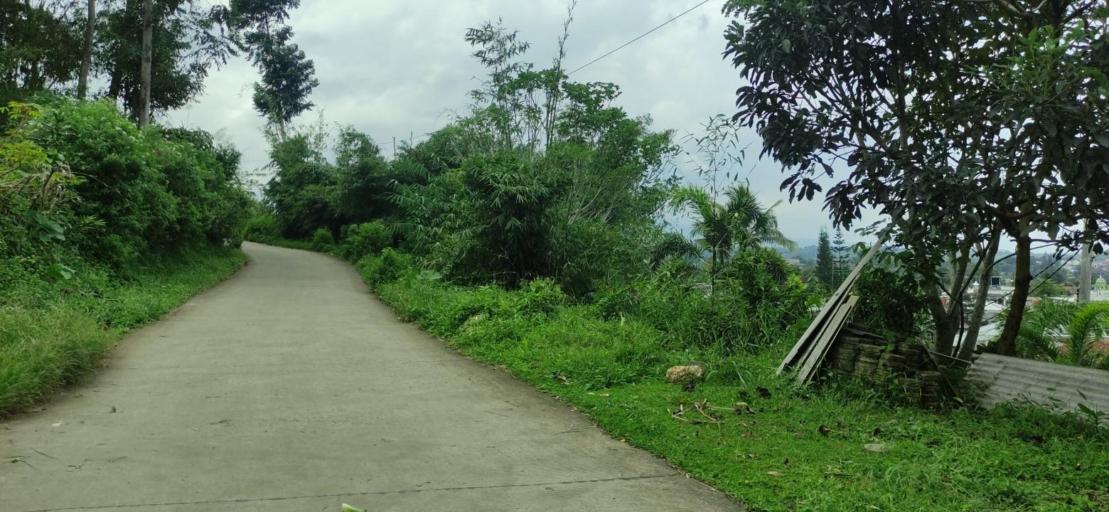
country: ID
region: West Java
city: Caringin
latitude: -6.6417
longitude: 106.8890
